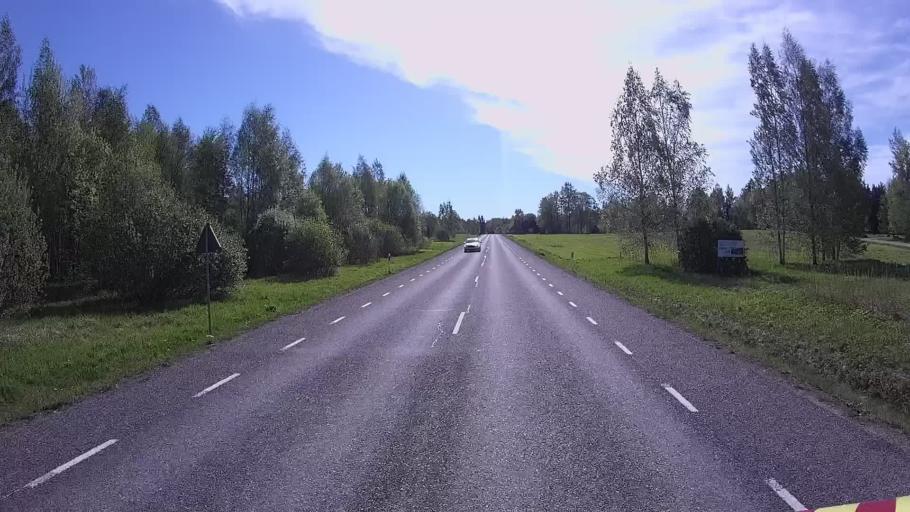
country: EE
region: Polvamaa
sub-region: Raepina vald
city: Rapina
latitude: 58.1012
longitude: 27.3788
